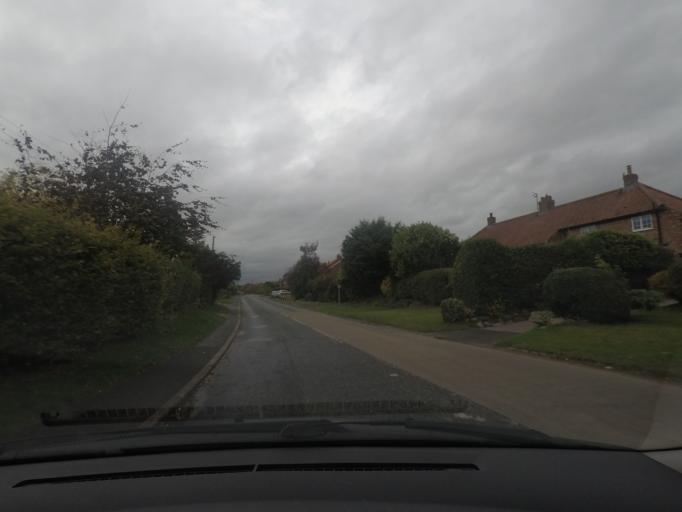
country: GB
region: England
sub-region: City of York
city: Wigginton
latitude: 54.0755
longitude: -1.1019
